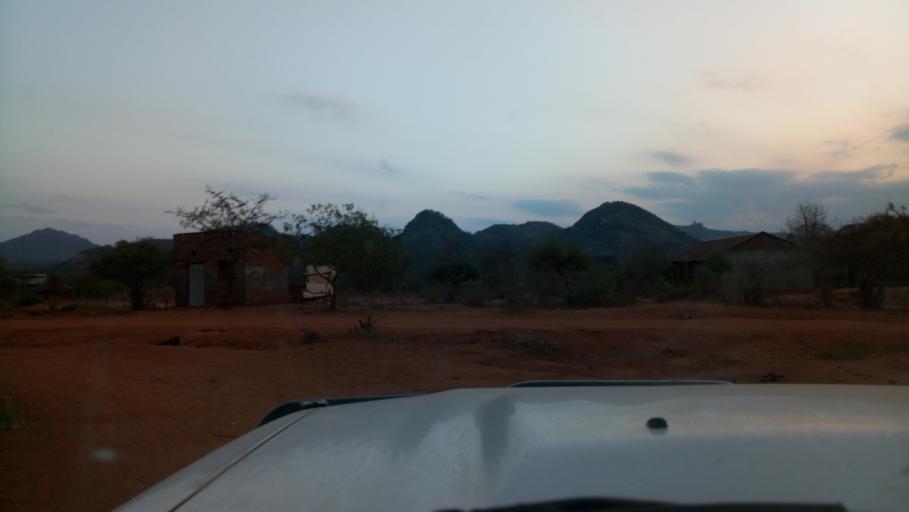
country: KE
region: Kitui
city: Kitui
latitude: -1.7148
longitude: 38.1902
